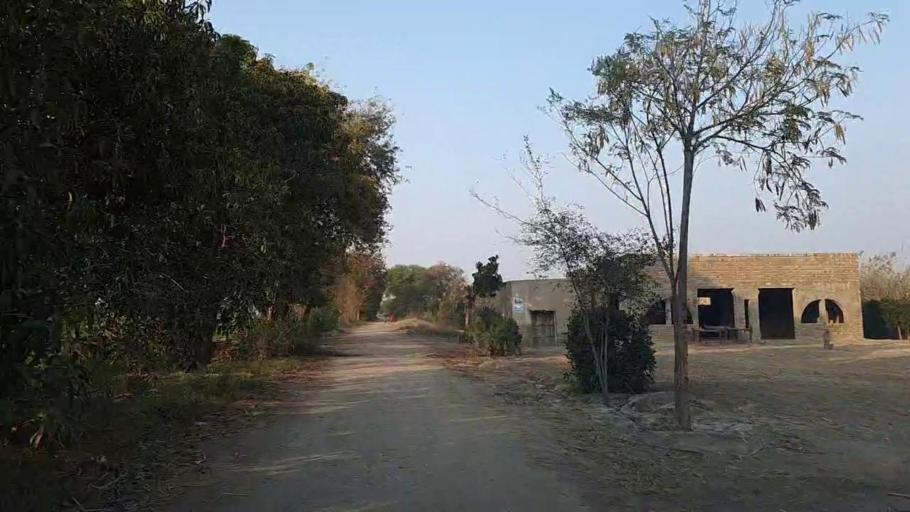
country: PK
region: Sindh
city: Daur
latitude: 26.4354
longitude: 68.3937
